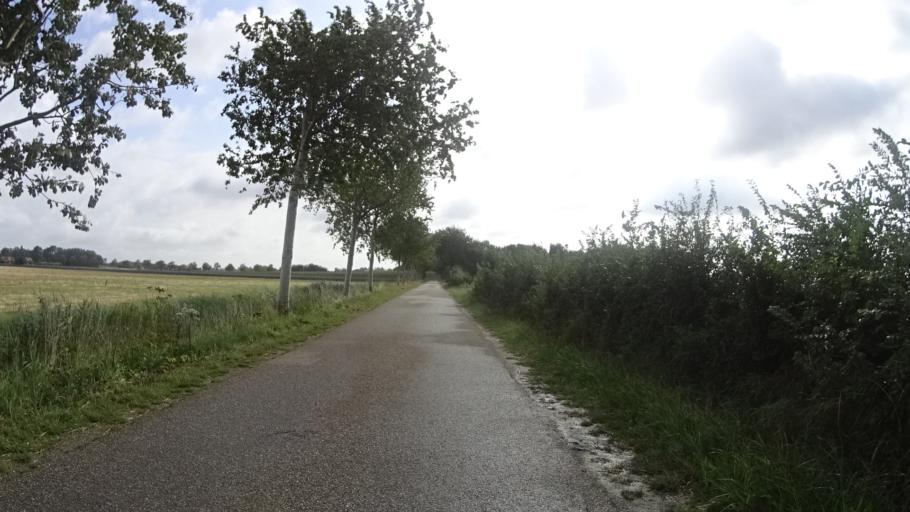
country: NL
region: Zeeland
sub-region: Schouwen-Duiveland
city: Scharendijke
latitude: 51.7238
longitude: 3.8153
